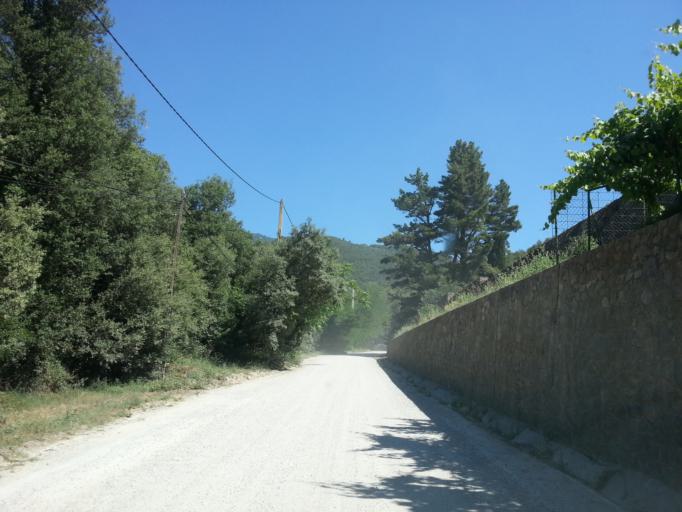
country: ES
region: Catalonia
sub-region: Provincia de Barcelona
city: Campins
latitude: 41.7359
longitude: 2.5013
